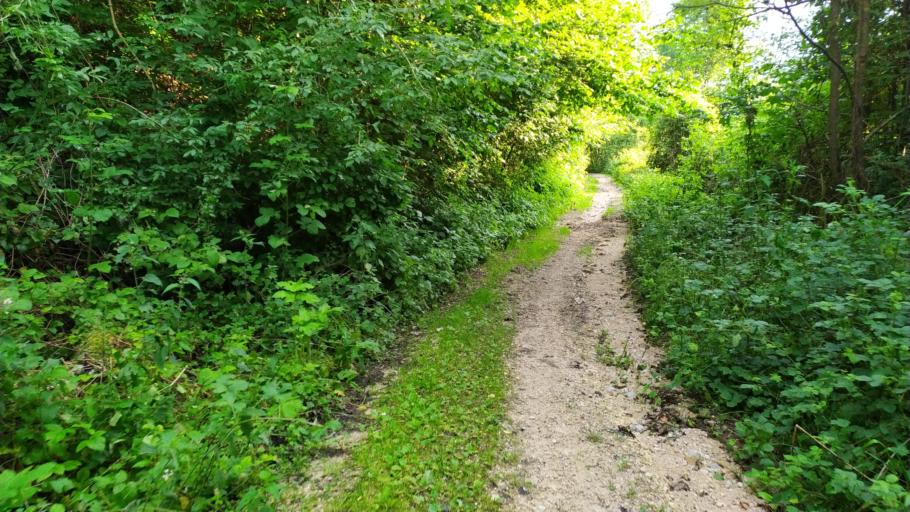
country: IT
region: Veneto
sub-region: Provincia di Vicenza
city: San Quirico
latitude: 45.6860
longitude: 11.2784
